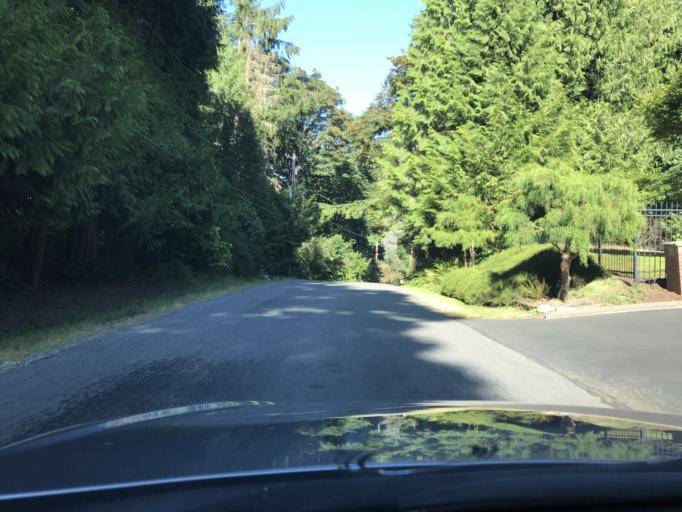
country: US
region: Washington
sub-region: King County
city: Maple Heights-Lake Desire
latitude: 47.4421
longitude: -122.0865
